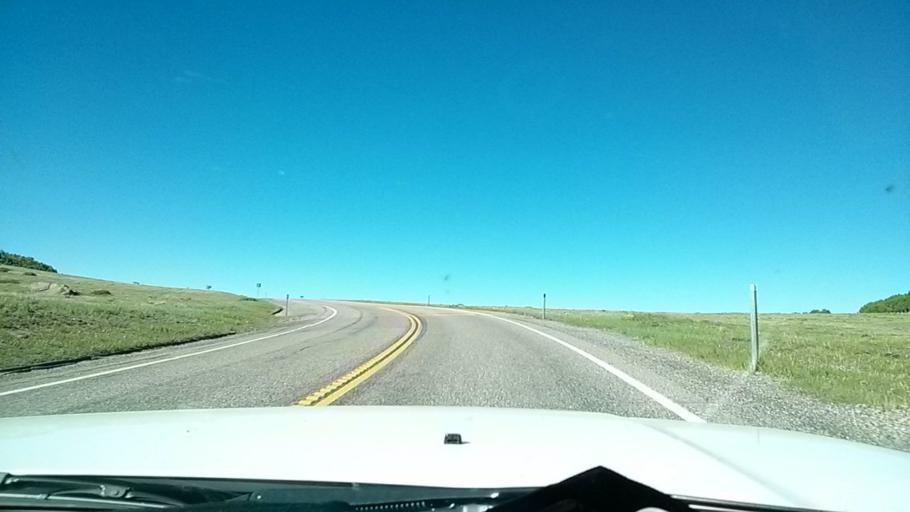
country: US
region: Utah
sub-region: Wayne County
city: Loa
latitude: 38.0341
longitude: -111.3330
